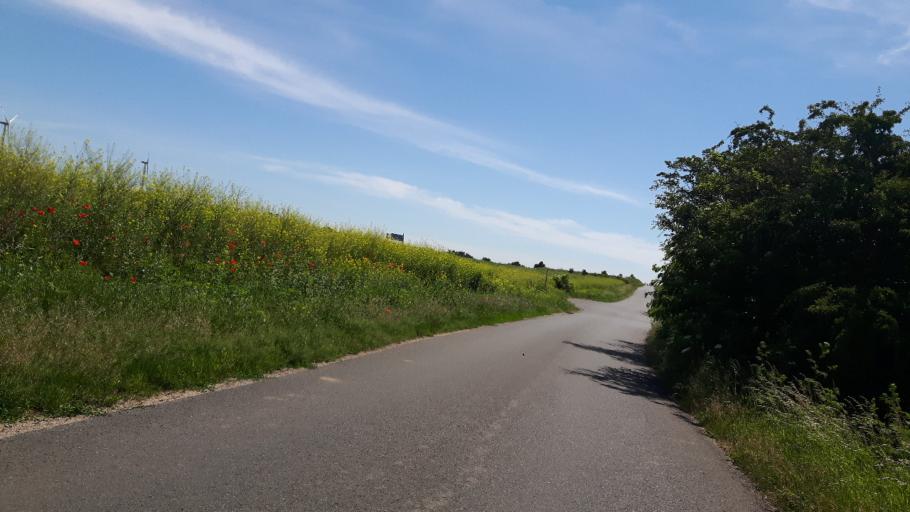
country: DE
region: Saxony-Anhalt
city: Grosskorbetha
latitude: 51.2323
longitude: 12.0492
